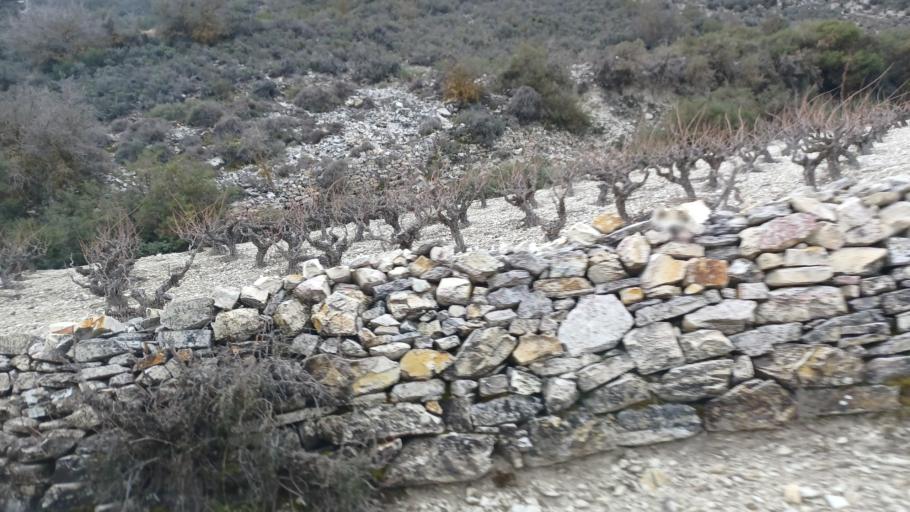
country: CY
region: Limassol
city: Pachna
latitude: 34.8687
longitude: 32.8003
